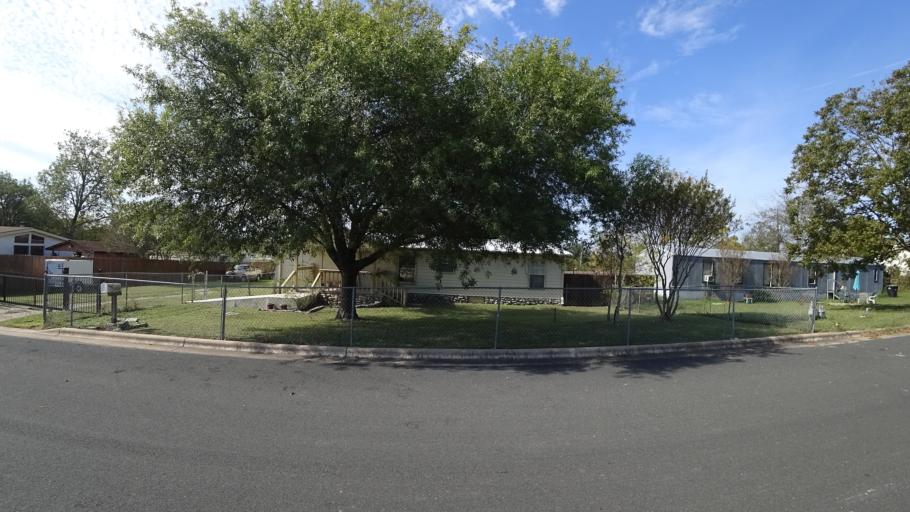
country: US
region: Texas
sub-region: Travis County
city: Pflugerville
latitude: 30.4131
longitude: -97.6326
